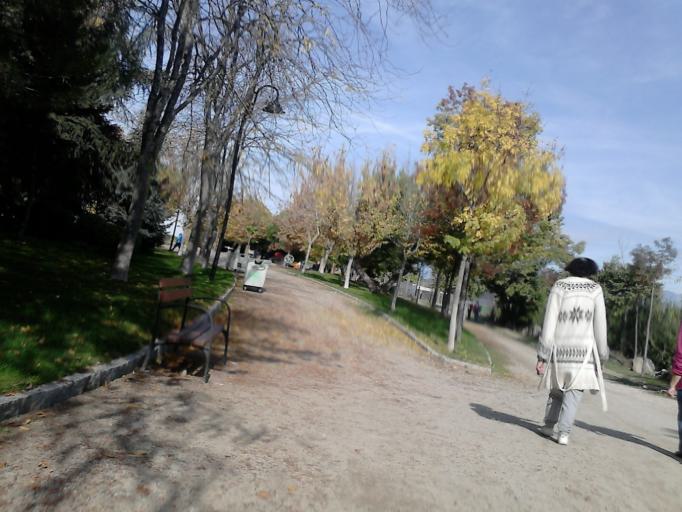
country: ES
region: Madrid
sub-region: Provincia de Madrid
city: Galapagar
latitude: 40.5824
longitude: -4.0059
